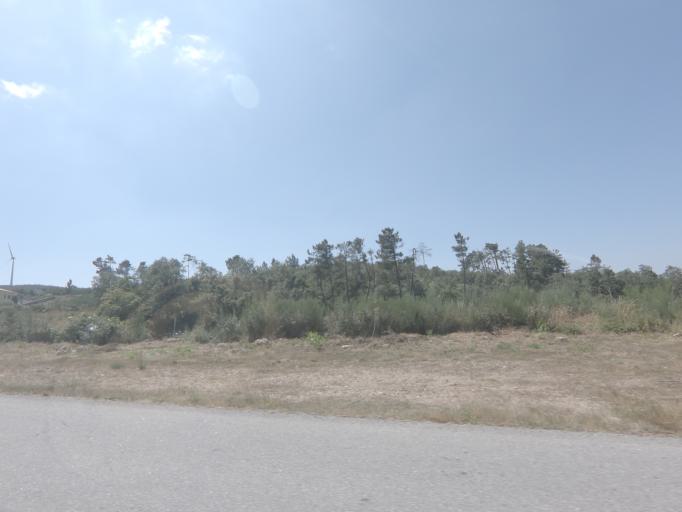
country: PT
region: Viseu
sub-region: Tarouca
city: Tarouca
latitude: 40.9906
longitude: -7.8268
